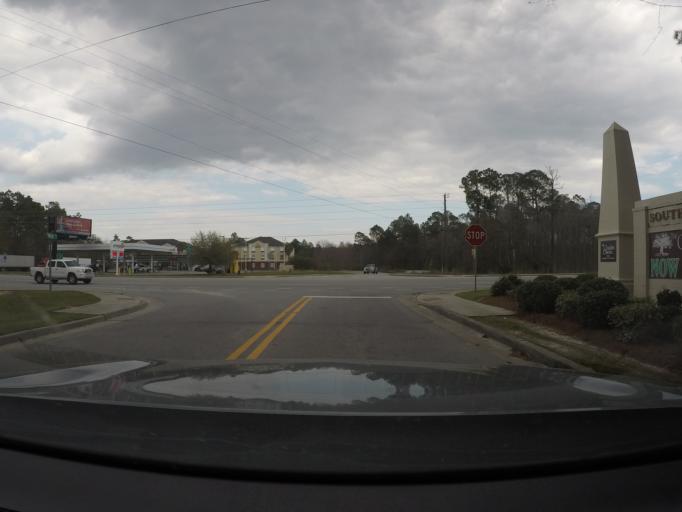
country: US
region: Georgia
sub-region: Bulloch County
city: Statesboro
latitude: 32.4059
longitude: -81.7626
